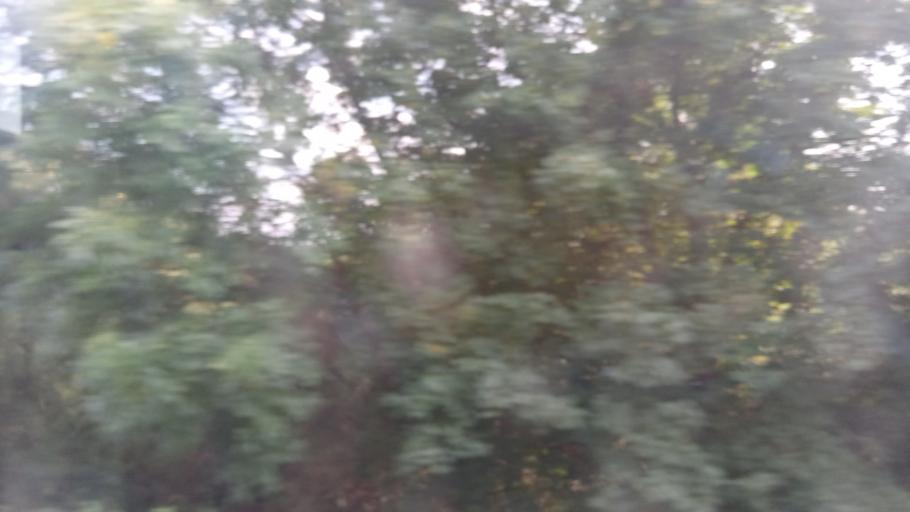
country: PL
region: Kujawsko-Pomorskie
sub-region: Powiat bydgoski
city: Biale Blota
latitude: 53.1529
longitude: 17.8706
